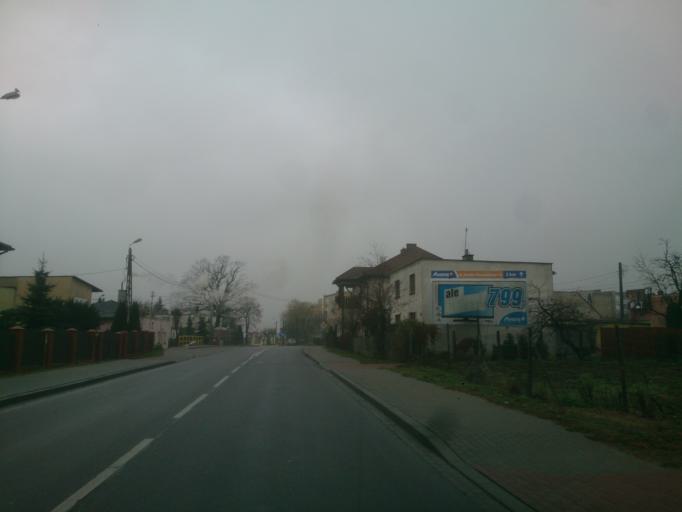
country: PL
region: Kujawsko-Pomorskie
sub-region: Powiat rypinski
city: Rypin
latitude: 53.0610
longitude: 19.4161
